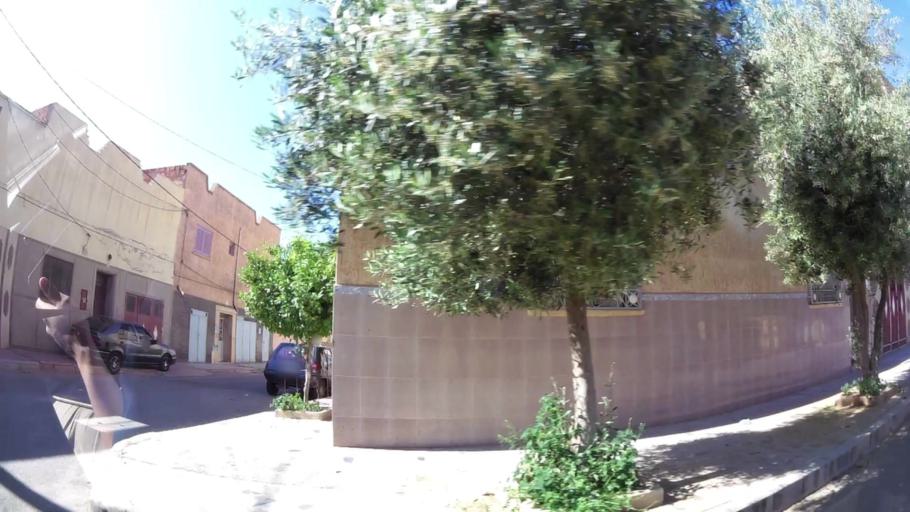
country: MA
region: Oriental
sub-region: Oujda-Angad
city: Oujda
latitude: 34.6877
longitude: -1.9226
